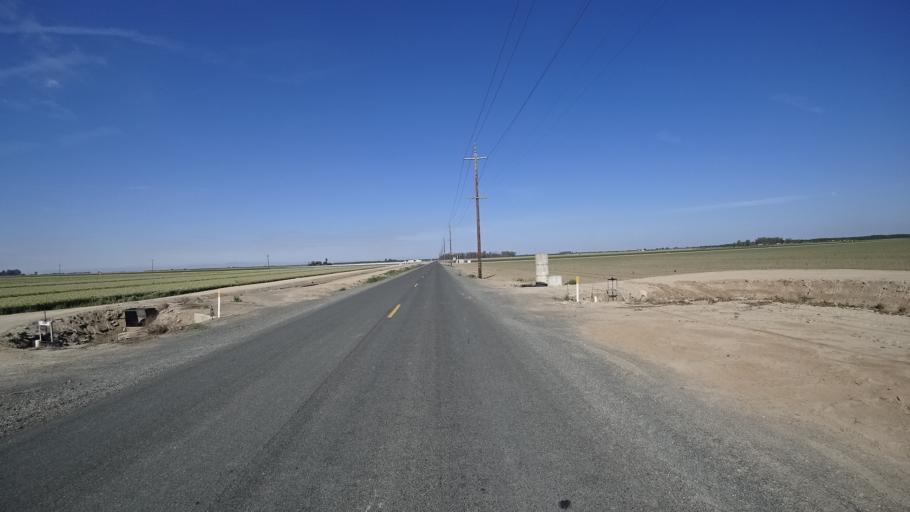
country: US
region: California
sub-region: Kings County
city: Home Garden
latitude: 36.2548
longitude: -119.6610
